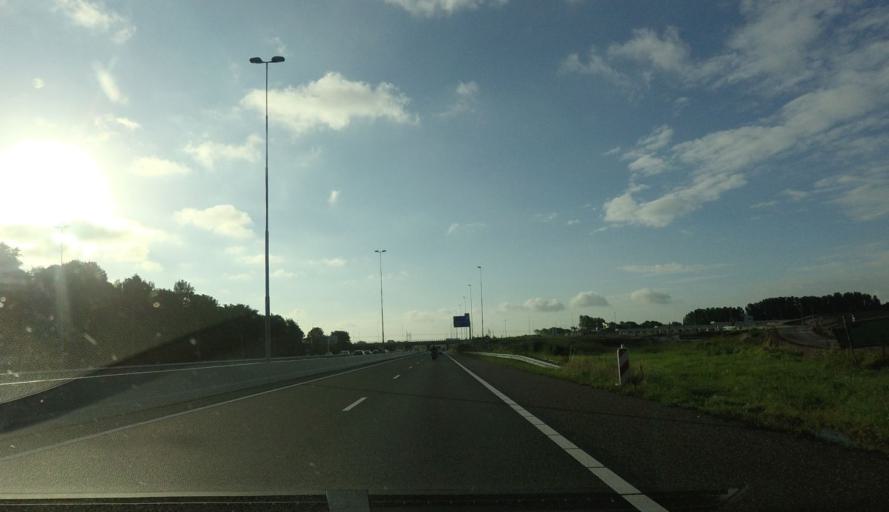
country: NL
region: North Holland
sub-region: Gemeente Aalsmeer
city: Aalsmeer
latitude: 52.3308
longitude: 4.7907
